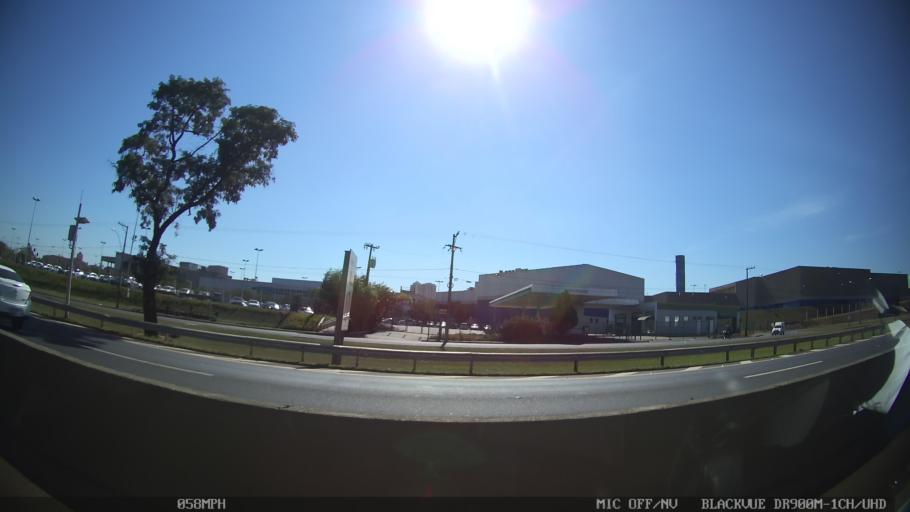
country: BR
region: Sao Paulo
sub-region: Ribeirao Preto
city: Ribeirao Preto
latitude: -21.2090
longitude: -47.7664
